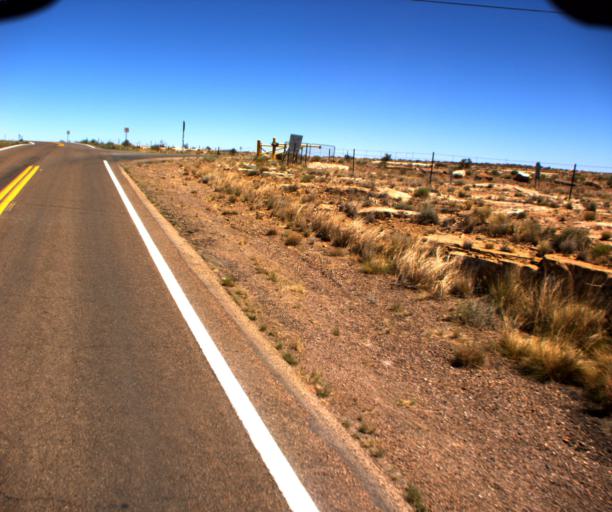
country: US
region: Arizona
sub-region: Navajo County
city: Winslow
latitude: 34.9692
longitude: -110.6471
